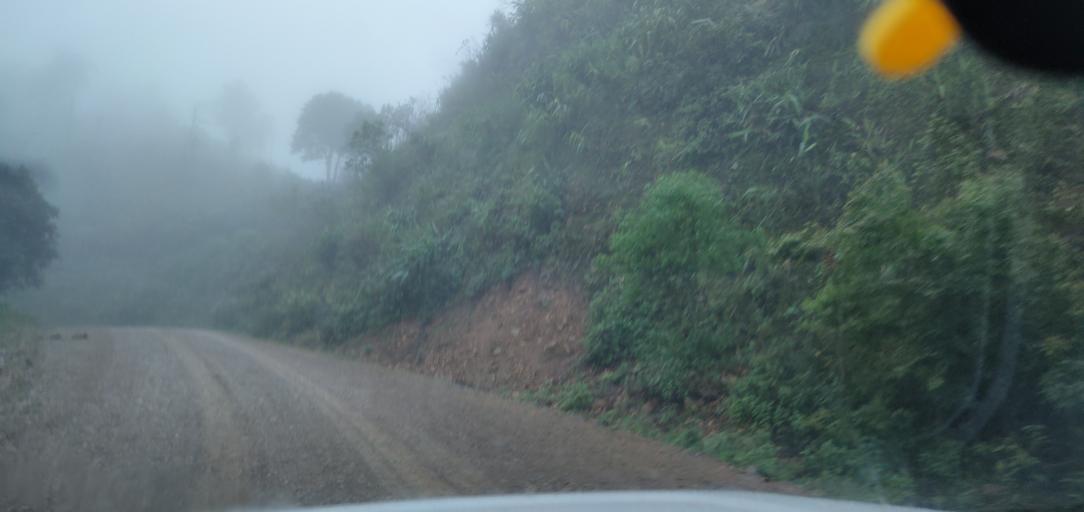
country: LA
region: Phongsali
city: Phongsali
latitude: 21.3947
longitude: 102.1913
